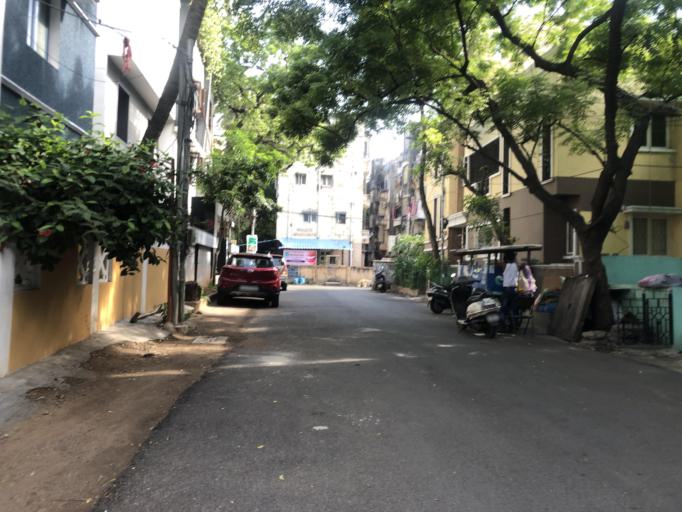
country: IN
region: Tamil Nadu
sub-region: Chennai
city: Gandhi Nagar
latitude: 13.0343
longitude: 80.2593
